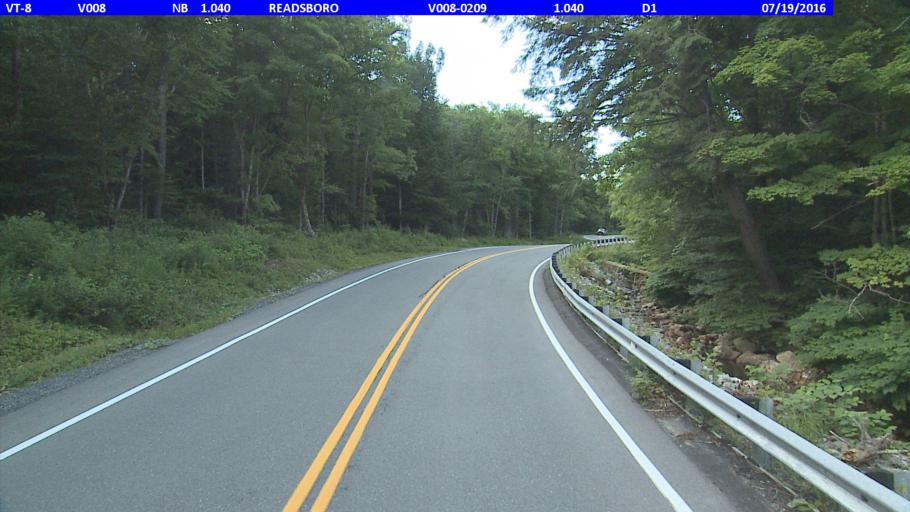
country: US
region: Massachusetts
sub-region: Berkshire County
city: North Adams
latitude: 42.8418
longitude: -72.9926
